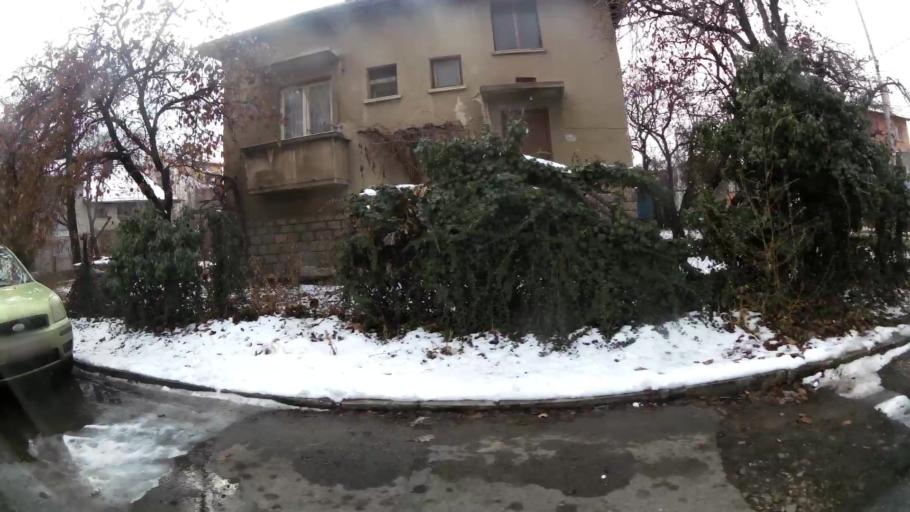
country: BG
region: Sofia-Capital
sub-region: Stolichna Obshtina
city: Sofia
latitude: 42.7010
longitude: 23.3799
